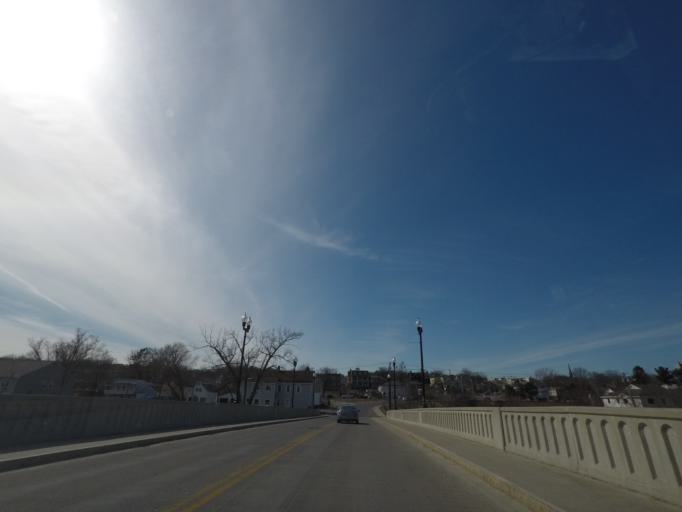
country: US
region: New York
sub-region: Albany County
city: Cohoes
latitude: 42.7682
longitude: -73.6959
